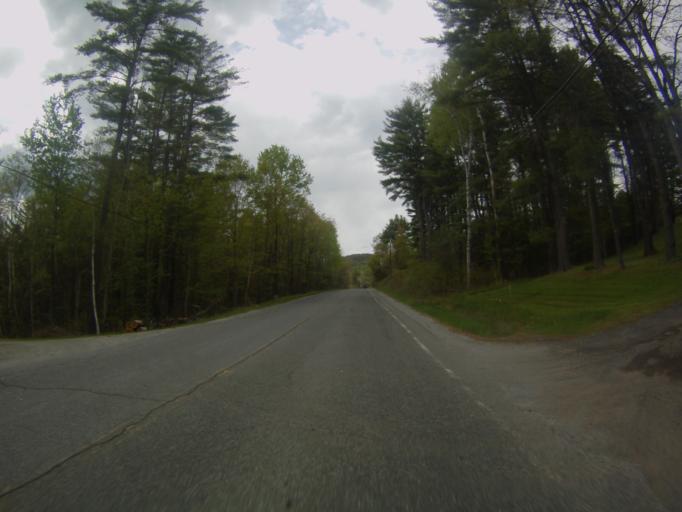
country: US
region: New York
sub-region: Essex County
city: Mineville
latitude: 44.0704
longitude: -73.5211
